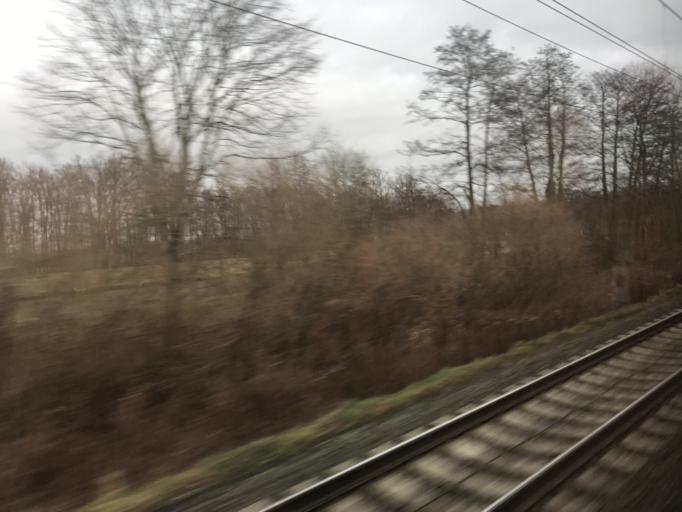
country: DE
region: Lower Saxony
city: Wolfsburg
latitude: 52.4304
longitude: 10.8224
